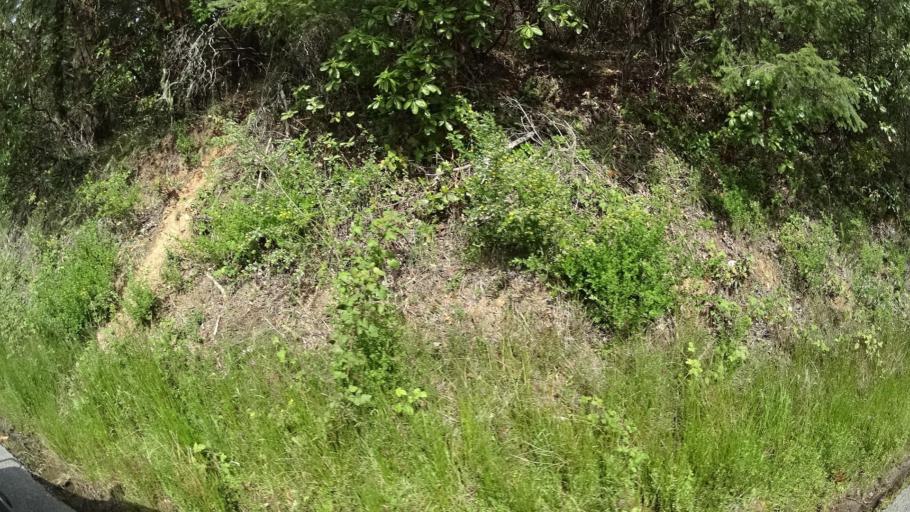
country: US
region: California
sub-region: Humboldt County
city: Redway
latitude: 40.1488
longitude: -123.6271
